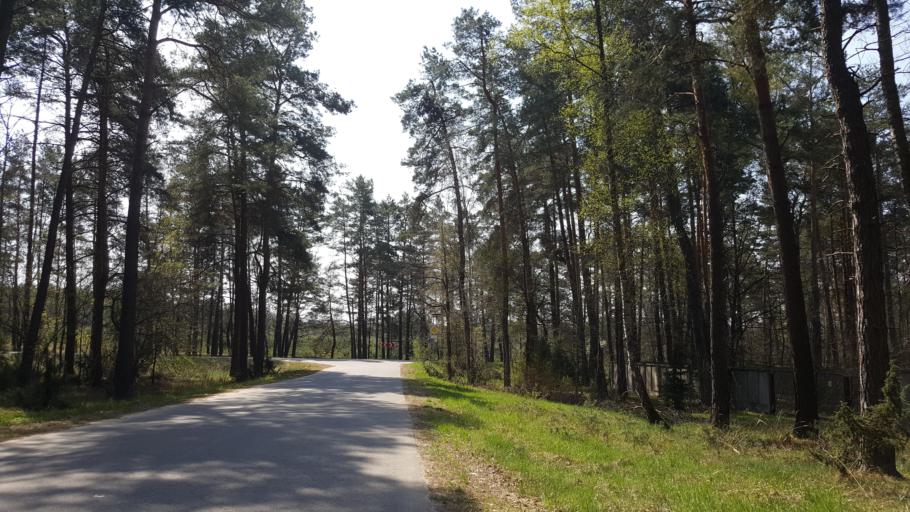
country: BY
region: Brest
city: Kamyanyets
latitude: 52.3483
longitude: 23.8279
